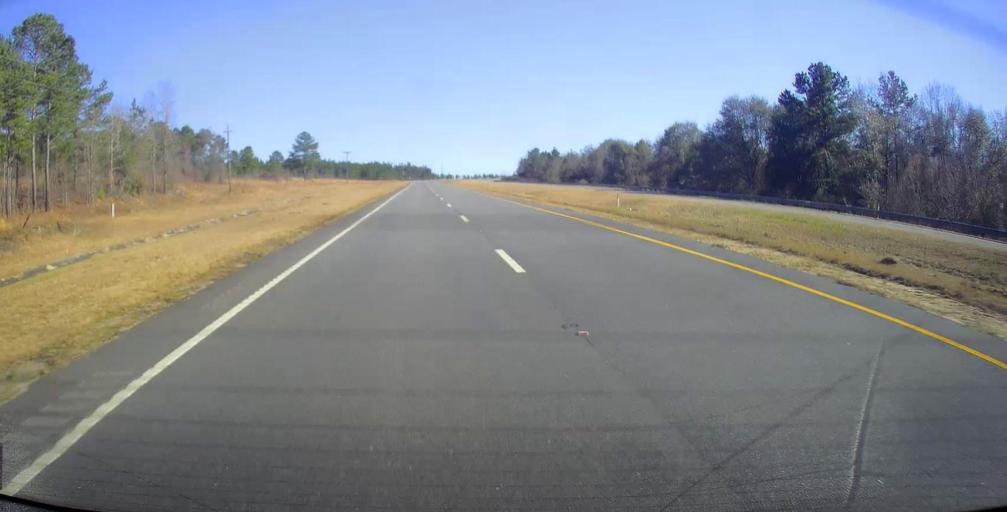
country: US
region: Georgia
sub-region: Taylor County
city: Butler
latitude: 32.6140
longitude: -84.2409
